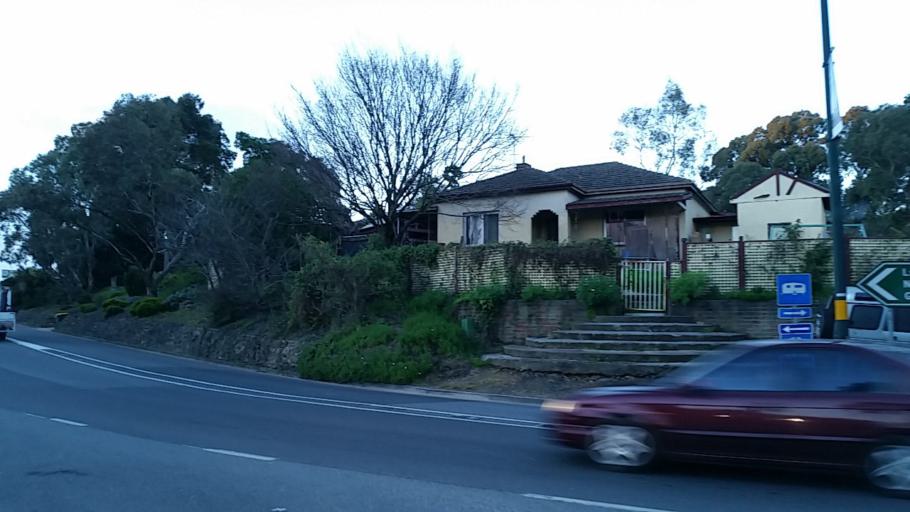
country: AU
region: South Australia
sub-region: Barossa
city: Williamstown
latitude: -34.6726
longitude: 138.8908
